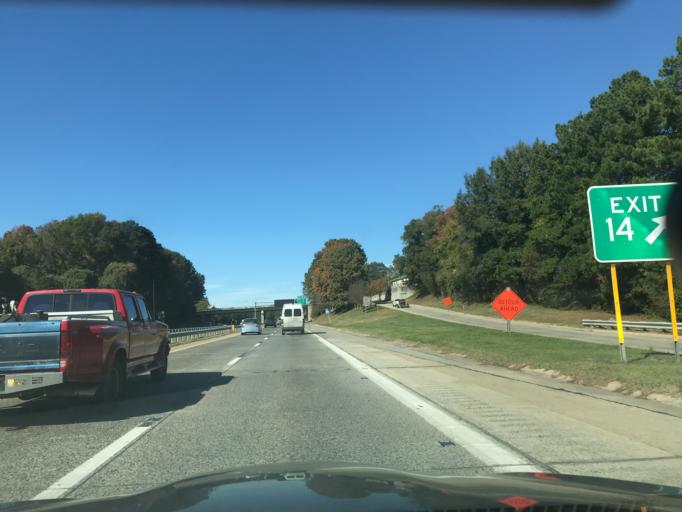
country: US
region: North Carolina
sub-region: Durham County
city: Durham
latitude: 36.0025
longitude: -78.9181
